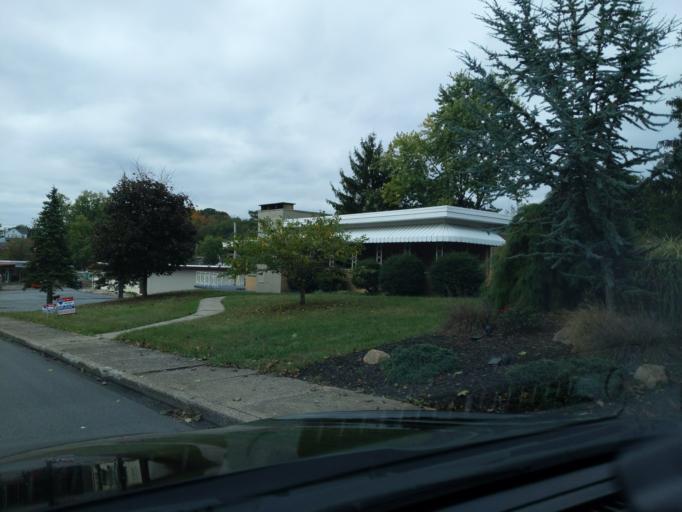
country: US
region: Pennsylvania
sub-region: Blair County
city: Lakemont
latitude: 40.4879
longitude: -78.4214
